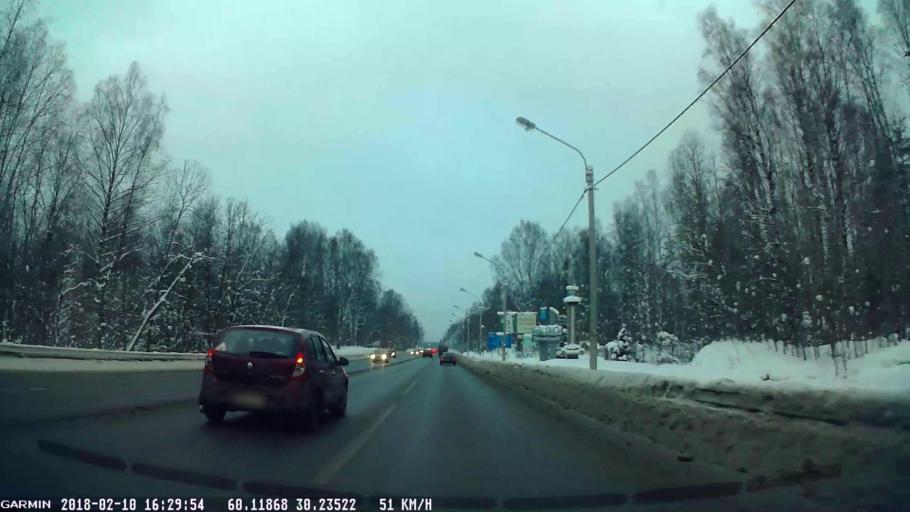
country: RU
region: St.-Petersburg
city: Levashovo
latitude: 60.1192
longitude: 30.2348
